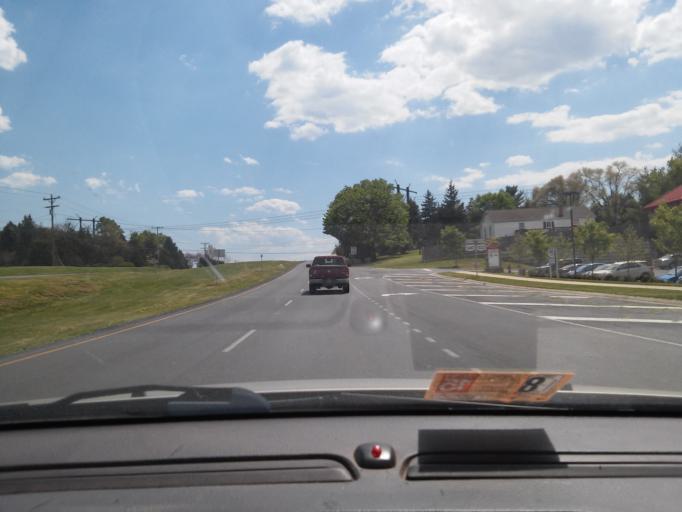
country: US
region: Virginia
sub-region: Warren County
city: Front Royal
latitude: 38.9770
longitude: -78.1851
